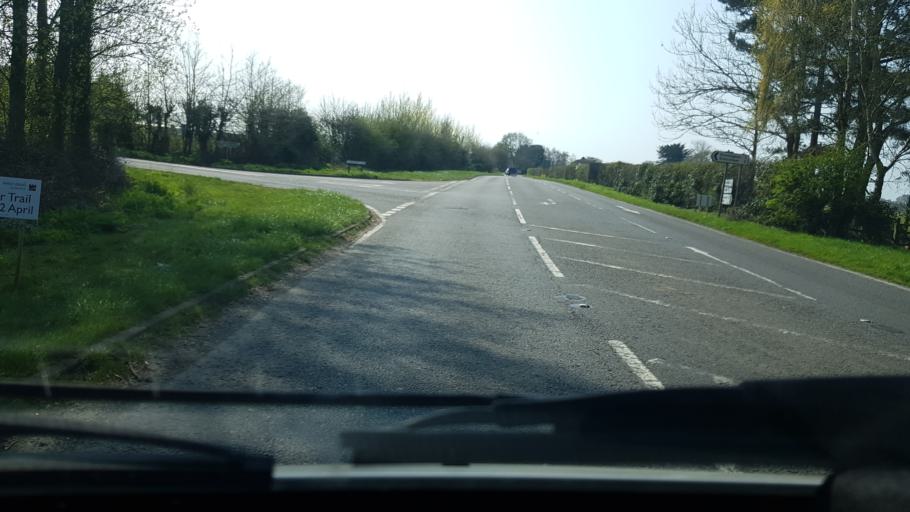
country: GB
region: England
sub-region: West Sussex
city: Birdham
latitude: 50.8048
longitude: -0.8066
